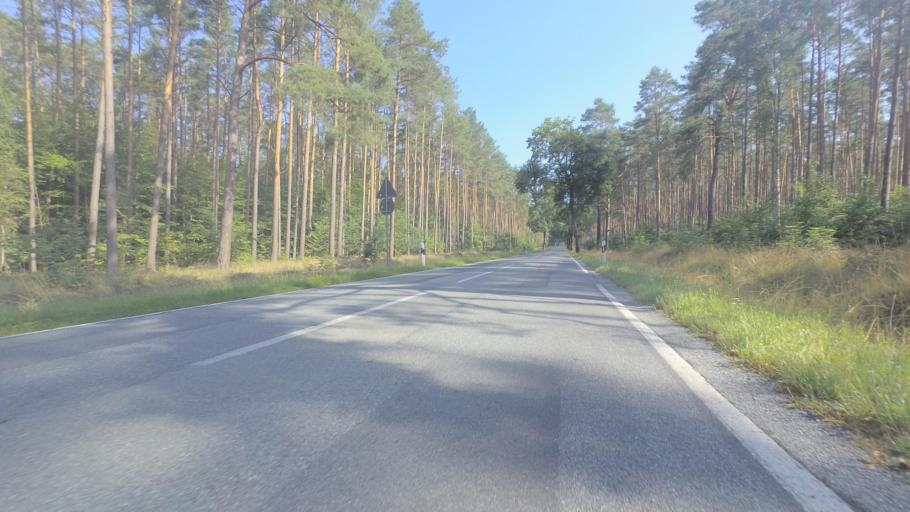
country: DE
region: Mecklenburg-Vorpommern
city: Malchow
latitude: 53.5508
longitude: 12.4480
